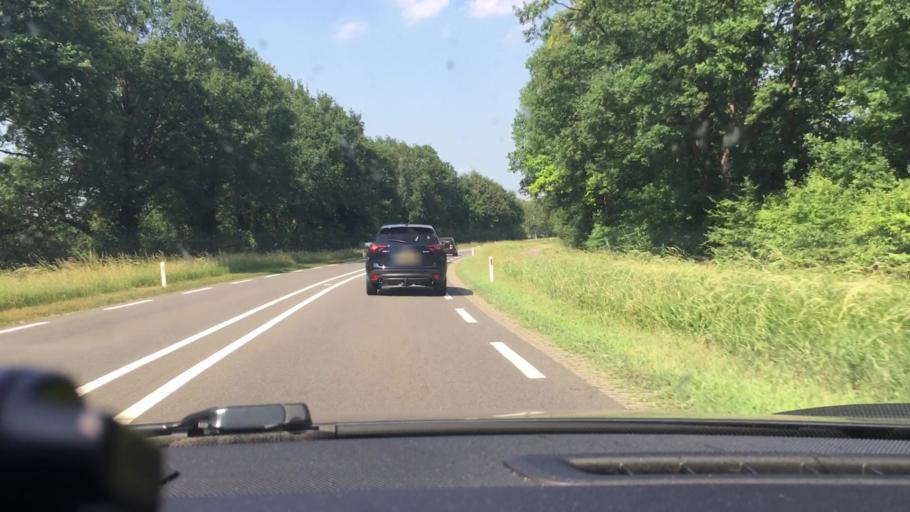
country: NL
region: Overijssel
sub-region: Gemeente Hof van Twente
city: Goor
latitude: 52.2324
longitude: 6.6052
